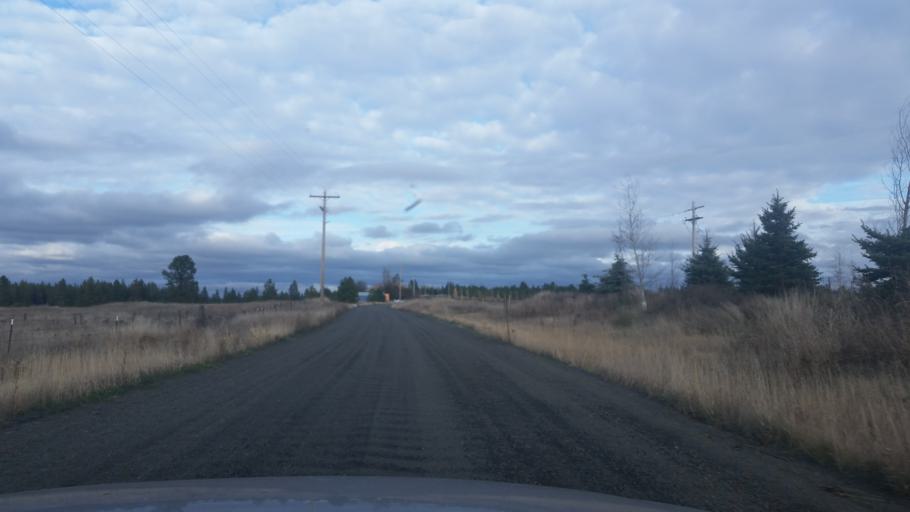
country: US
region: Washington
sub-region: Spokane County
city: Cheney
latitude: 47.4196
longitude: -117.4735
